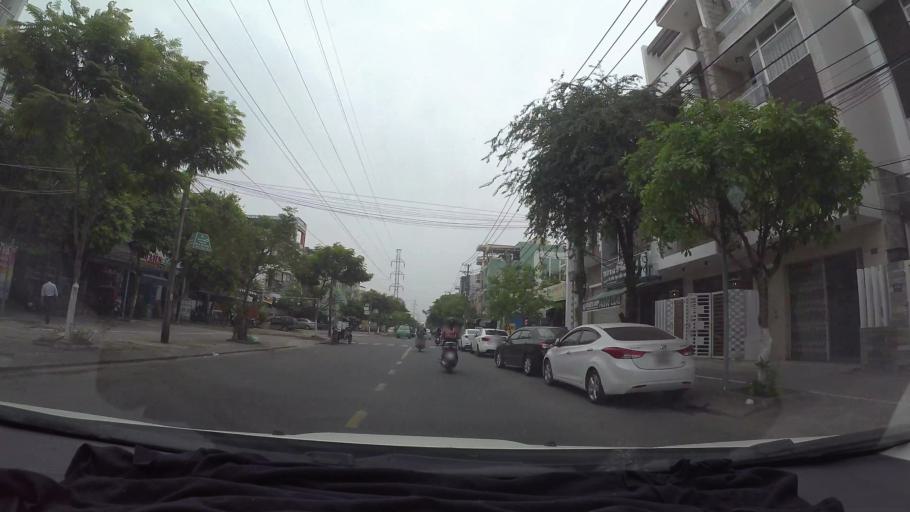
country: VN
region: Da Nang
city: Cam Le
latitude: 16.0388
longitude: 108.2180
